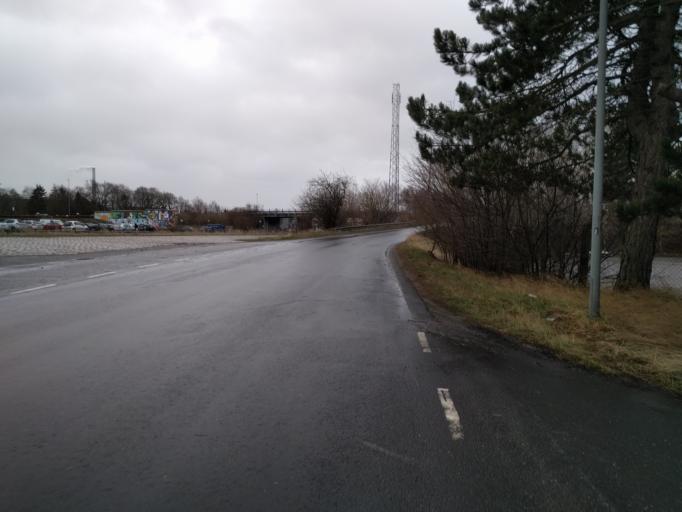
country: DK
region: Central Jutland
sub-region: Randers Kommune
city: Randers
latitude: 56.4596
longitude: 10.0275
